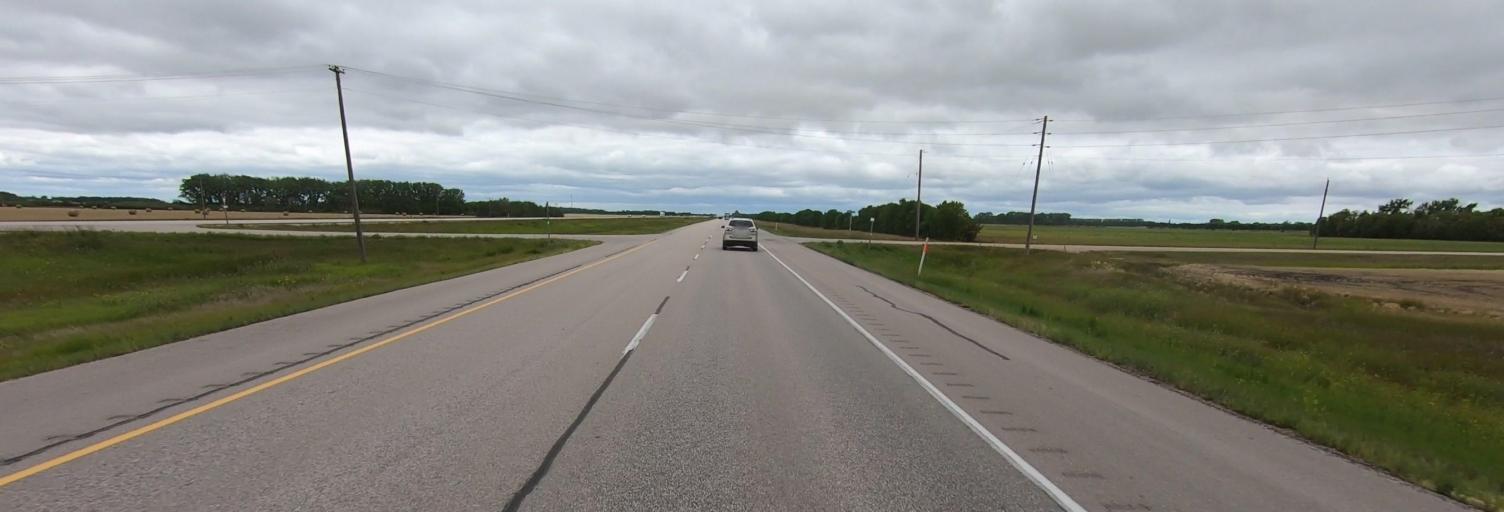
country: CA
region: Manitoba
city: Portage la Prairie
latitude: 49.9448
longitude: -97.9632
